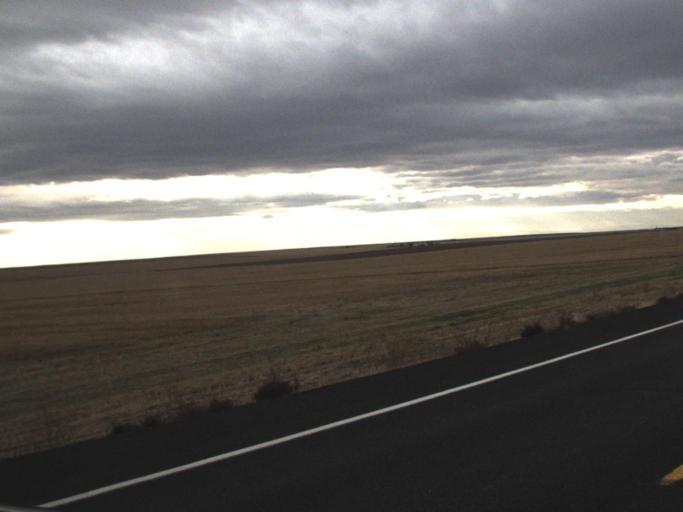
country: US
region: Washington
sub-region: Franklin County
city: Connell
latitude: 46.7945
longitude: -118.6116
